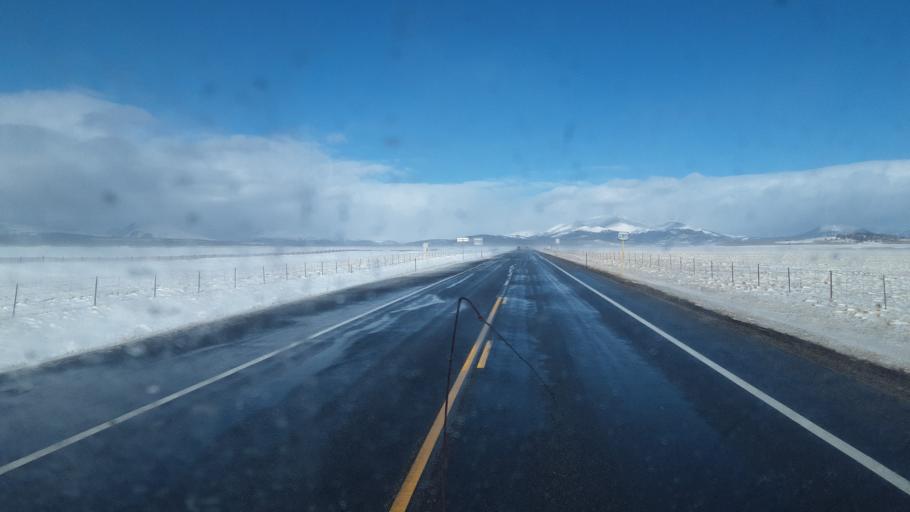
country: US
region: Colorado
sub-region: Park County
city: Fairplay
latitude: 39.1539
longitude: -105.9992
